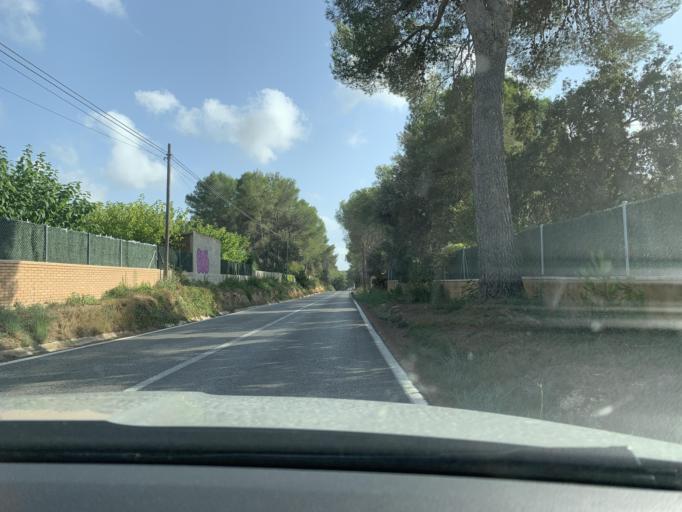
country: ES
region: Catalonia
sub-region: Provincia de Tarragona
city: el Catllar
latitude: 41.1589
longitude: 1.3153
